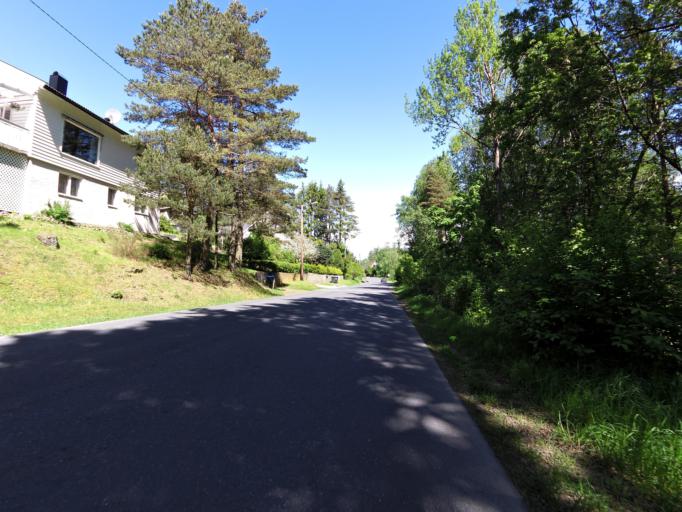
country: NO
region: Ostfold
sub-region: Fredrikstad
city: Fredrikstad
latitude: 59.2240
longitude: 10.9638
